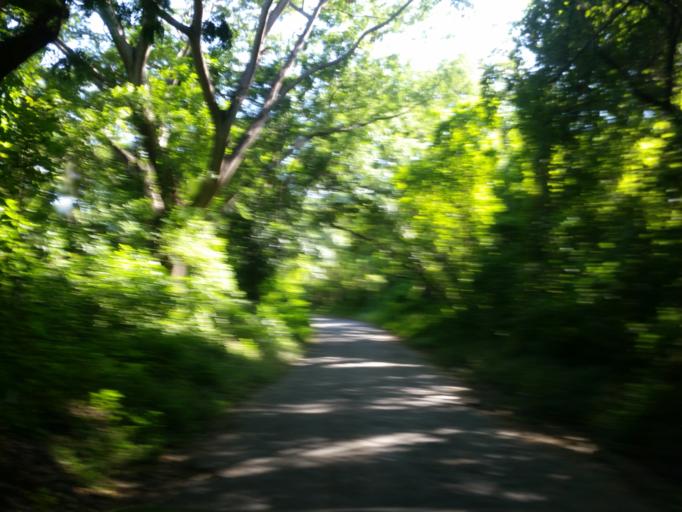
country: NI
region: Masaya
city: Catarina
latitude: 11.9324
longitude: -86.0566
